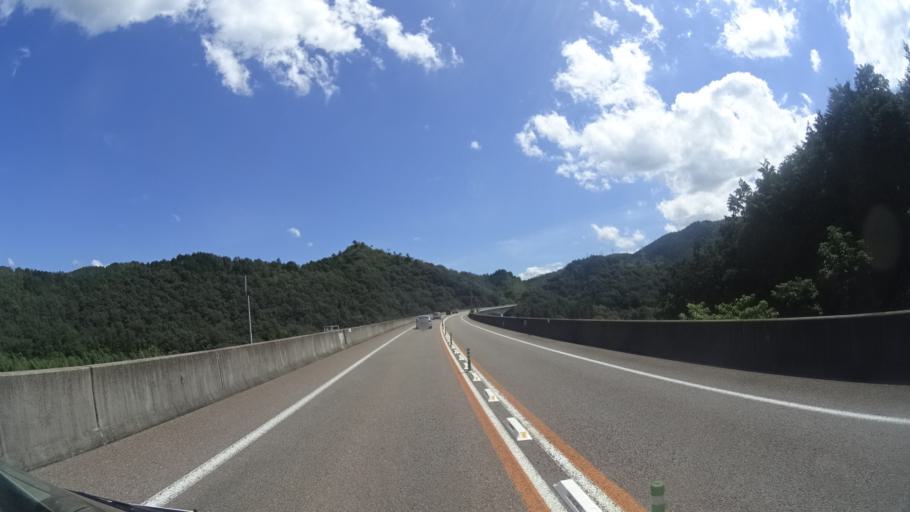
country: JP
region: Gifu
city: Minokamo
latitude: 35.5083
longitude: 136.9803
